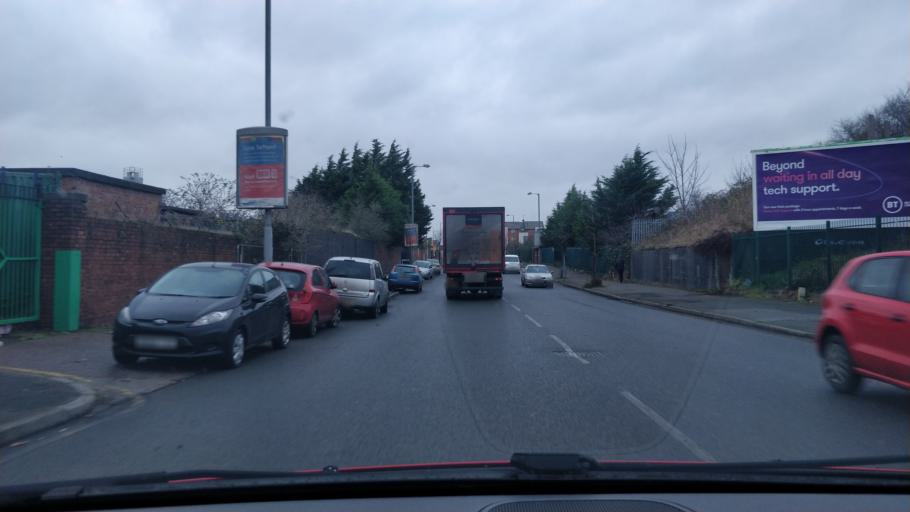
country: GB
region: England
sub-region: Sefton
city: Litherland
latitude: 53.4577
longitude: -2.9845
